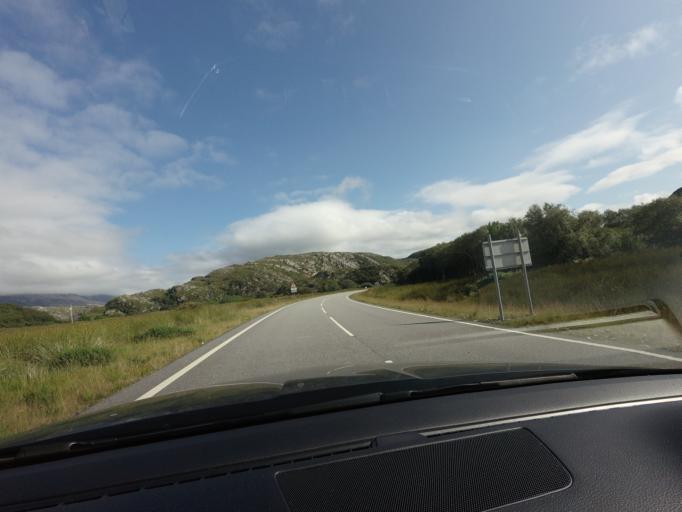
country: GB
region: Scotland
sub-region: Highland
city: Ullapool
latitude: 58.3769
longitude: -5.0178
